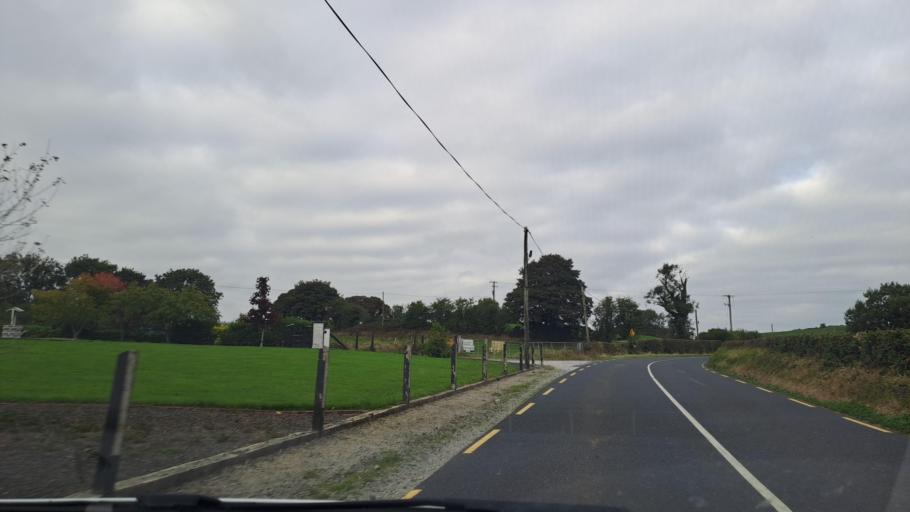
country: IE
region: Ulster
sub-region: County Monaghan
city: Carrickmacross
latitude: 54.0268
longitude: -6.7785
